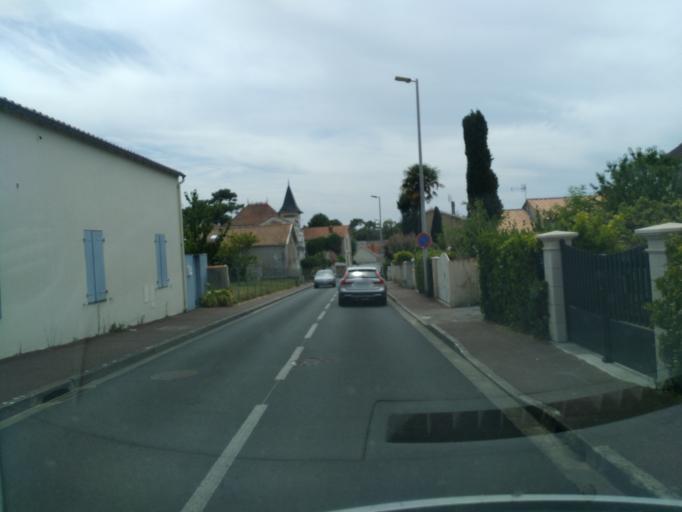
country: FR
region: Poitou-Charentes
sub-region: Departement de la Charente-Maritime
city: Saint-Palais-sur-Mer
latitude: 45.6446
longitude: -1.0849
